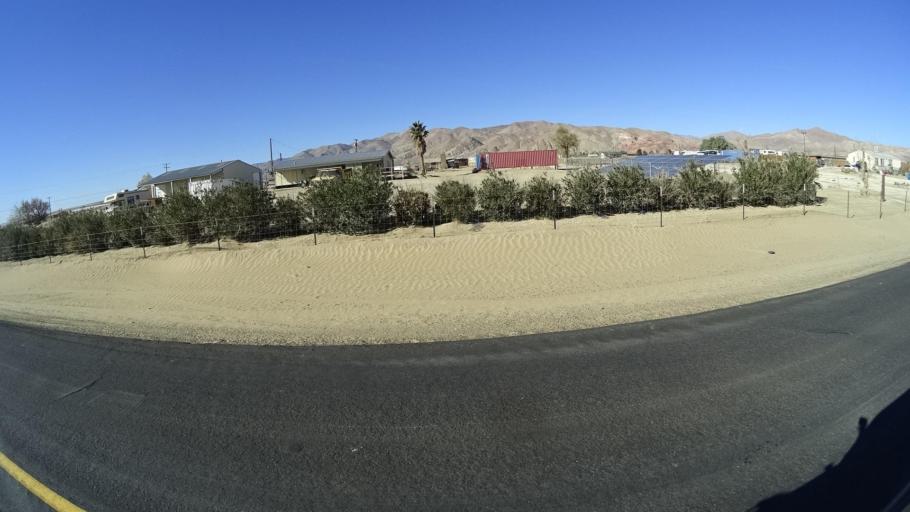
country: US
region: California
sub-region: Kern County
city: California City
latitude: 35.2819
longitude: -117.9858
